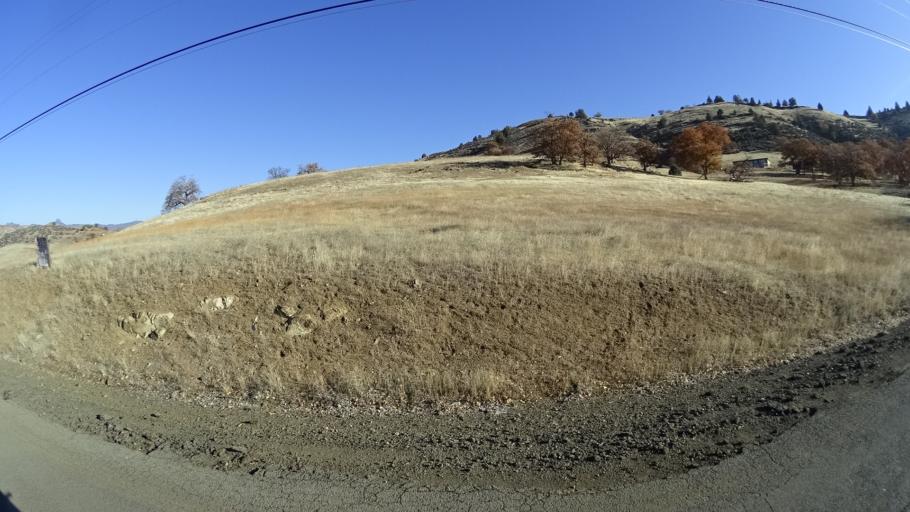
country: US
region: California
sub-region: Siskiyou County
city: Montague
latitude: 41.8852
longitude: -122.4739
